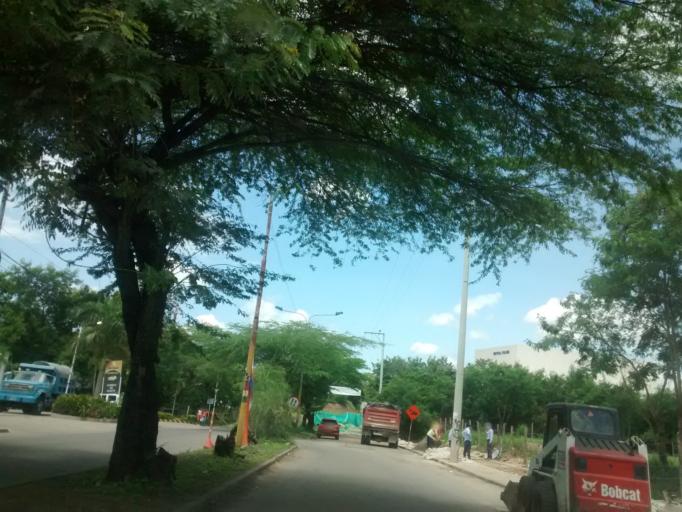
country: CO
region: Cundinamarca
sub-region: Girardot
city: Girardot City
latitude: 4.3080
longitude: -74.7953
